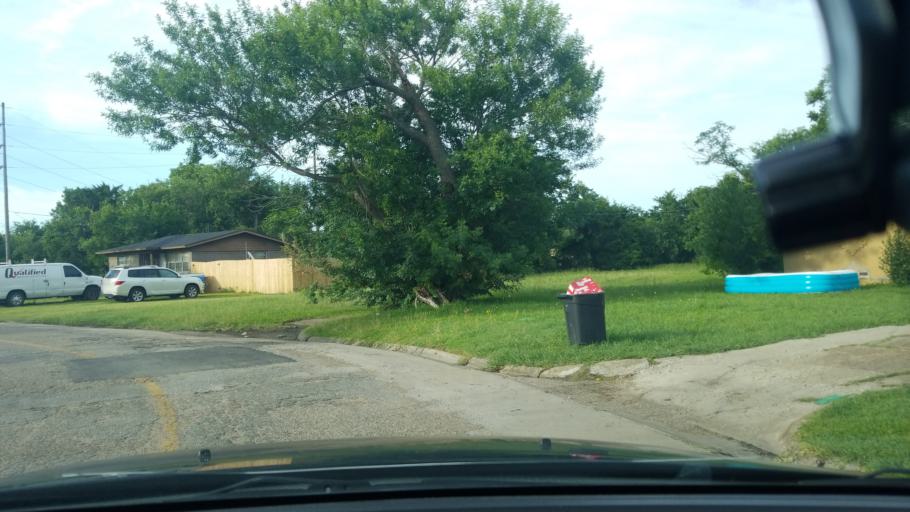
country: US
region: Texas
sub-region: Dallas County
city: Balch Springs
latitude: 32.7545
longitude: -96.6268
